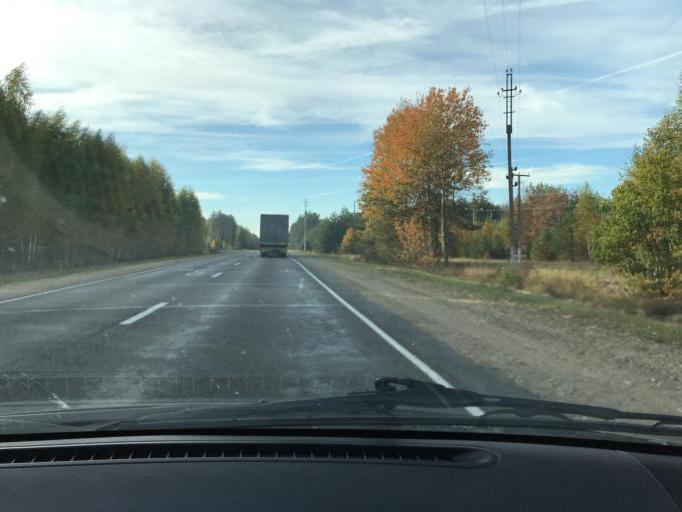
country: BY
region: Brest
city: Horad Pinsk
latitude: 52.1507
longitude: 25.8530
